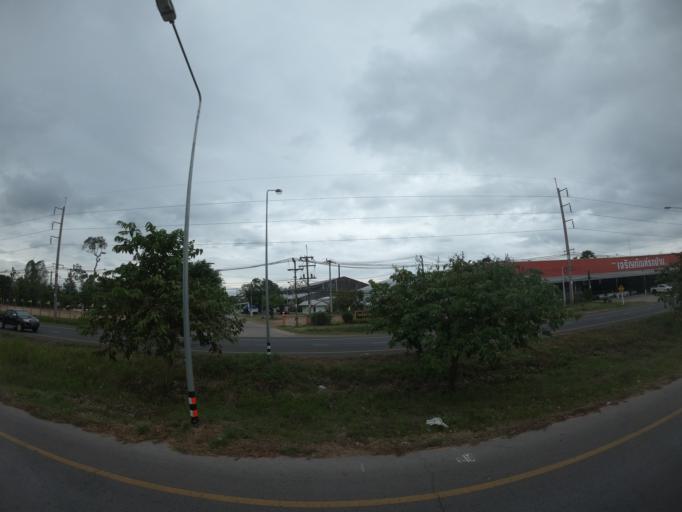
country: TH
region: Roi Et
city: Roi Et
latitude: 16.0440
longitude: 103.6290
